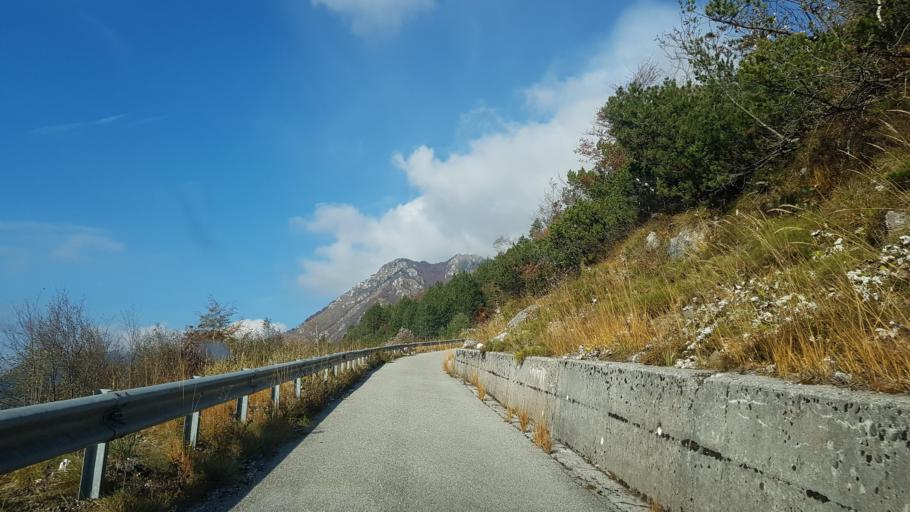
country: IT
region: Friuli Venezia Giulia
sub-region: Provincia di Udine
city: Moggio Udinese
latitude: 46.4563
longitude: 13.2066
